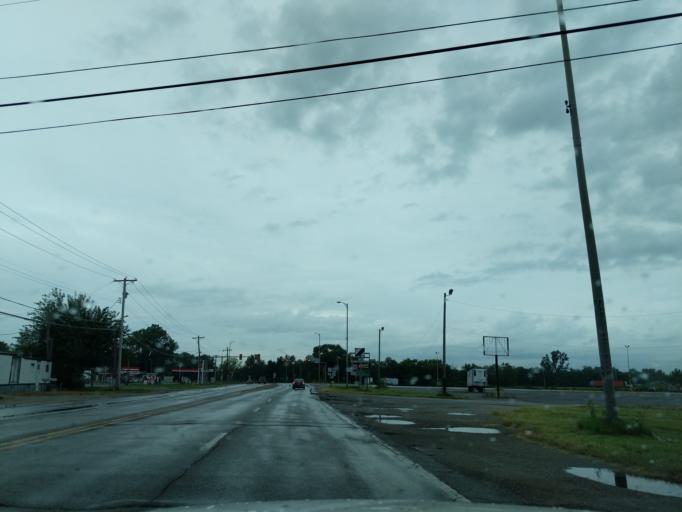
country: US
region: Illinois
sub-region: Saint Clair County
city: Fairmont City
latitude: 38.6593
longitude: -90.0905
